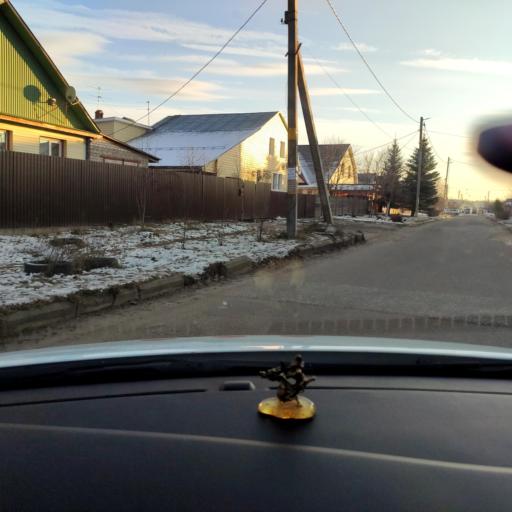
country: RU
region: Tatarstan
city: Stolbishchi
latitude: 55.6124
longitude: 49.1368
